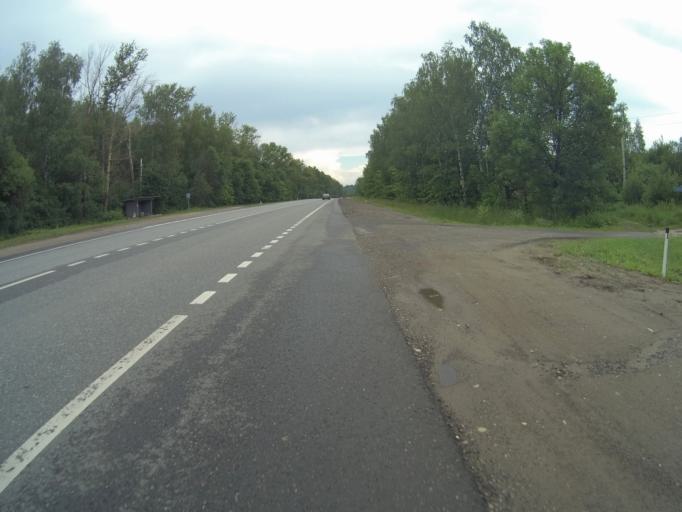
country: RU
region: Vladimir
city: Kameshkovo
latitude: 56.1965
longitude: 40.8746
